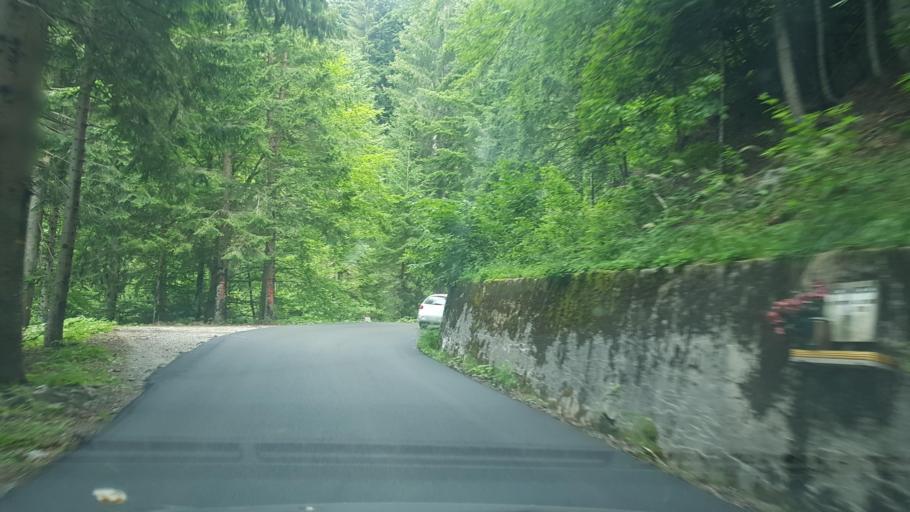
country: IT
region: Friuli Venezia Giulia
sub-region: Provincia di Udine
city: Paularo
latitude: 46.5604
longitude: 13.1241
